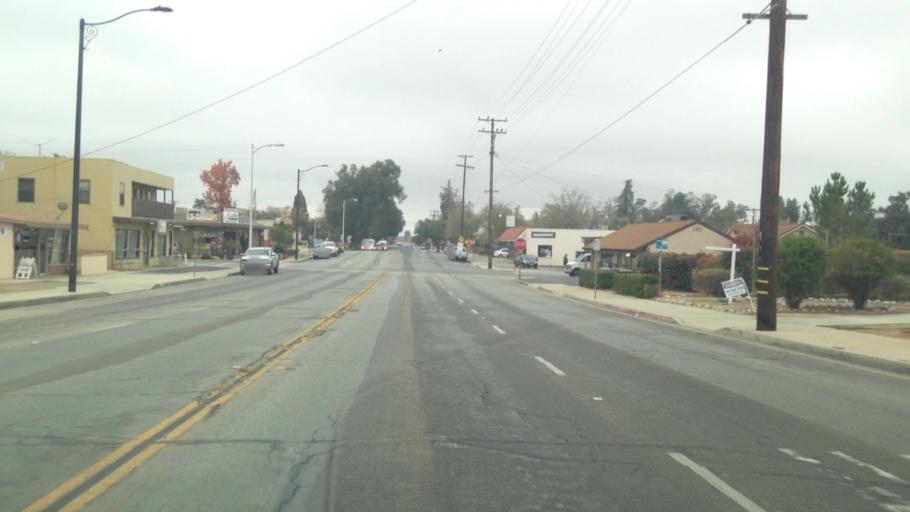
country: US
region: California
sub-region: Riverside County
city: Beaumont
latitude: 33.9364
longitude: -116.9772
